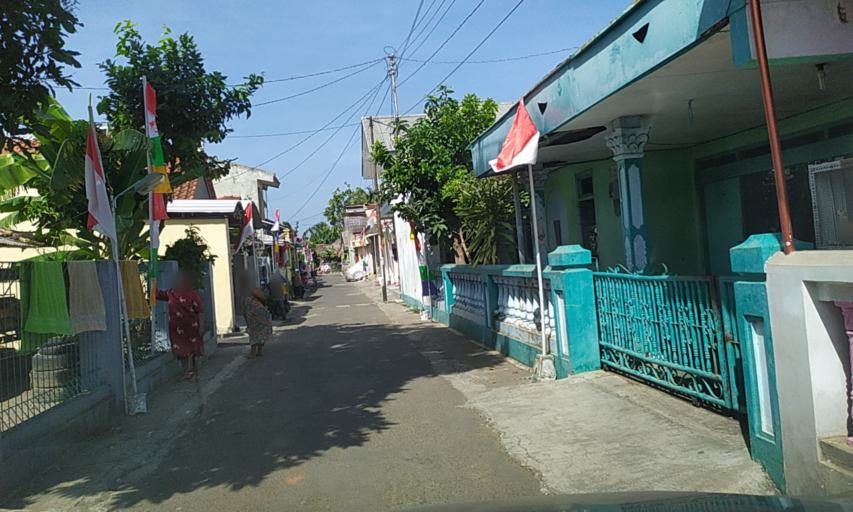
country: ID
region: Central Java
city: Karangbadar Kidul
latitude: -7.7157
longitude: 109.0085
